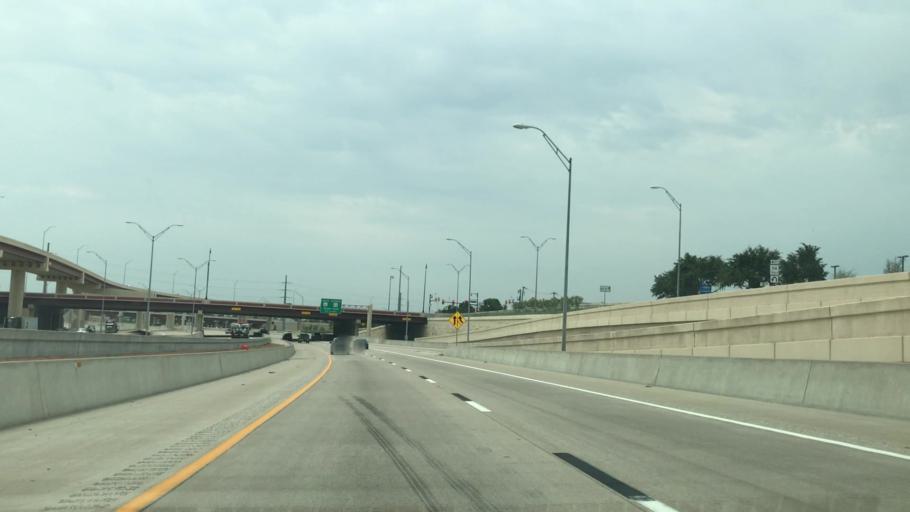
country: US
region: Texas
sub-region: Tarrant County
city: Grapevine
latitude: 32.9264
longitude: -97.0907
